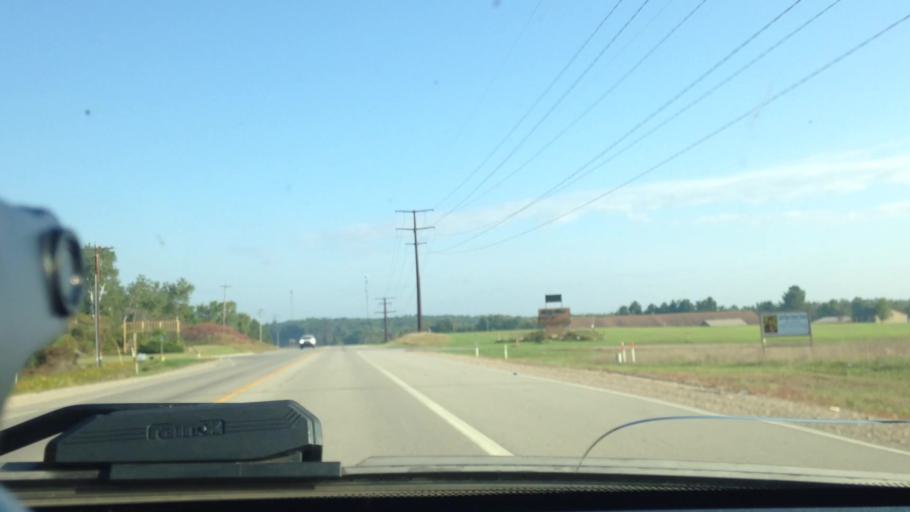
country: US
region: Wisconsin
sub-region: Marinette County
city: Peshtigo
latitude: 45.2021
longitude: -87.9943
